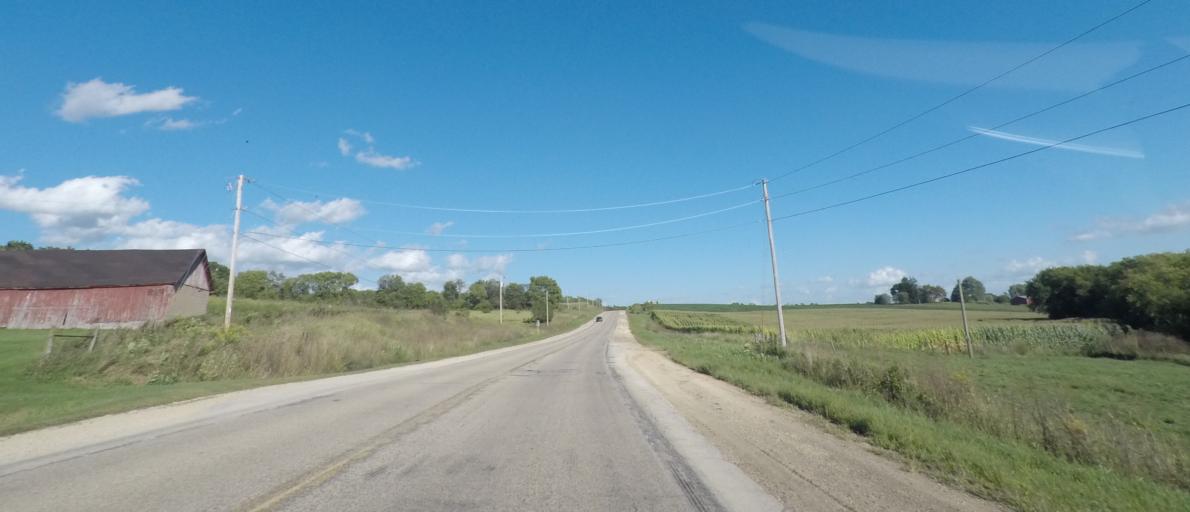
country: US
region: Wisconsin
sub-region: Iowa County
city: Dodgeville
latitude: 42.9814
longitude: -90.0762
